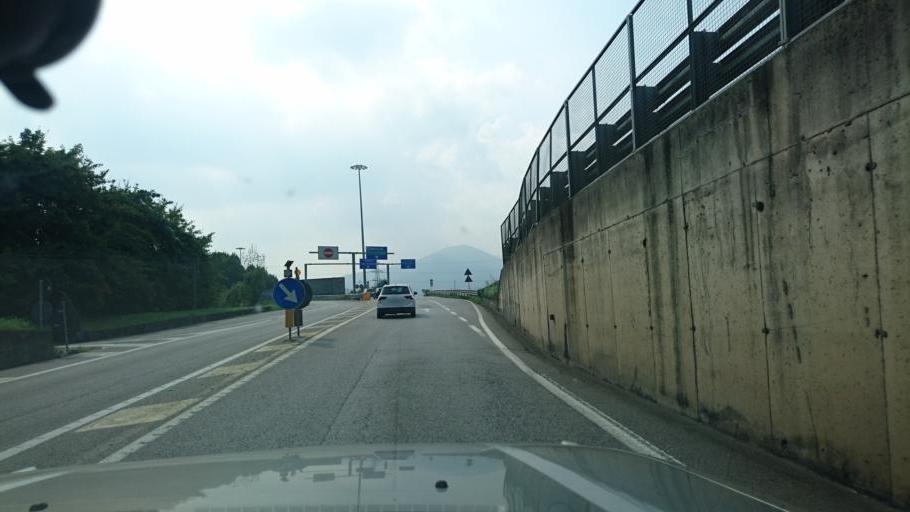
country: IT
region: Lombardy
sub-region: Provincia di Brescia
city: San Giacomo
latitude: 45.6061
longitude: 10.4679
